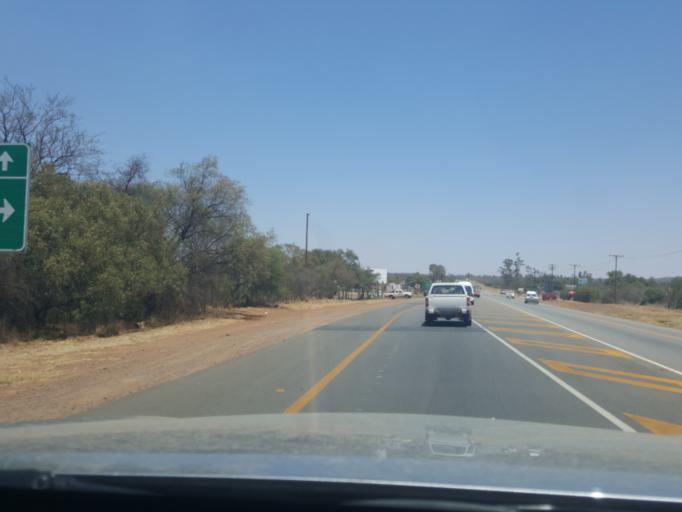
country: ZA
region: North-West
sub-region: Ngaka Modiri Molema District Municipality
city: Zeerust
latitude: -25.5590
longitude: 26.0643
